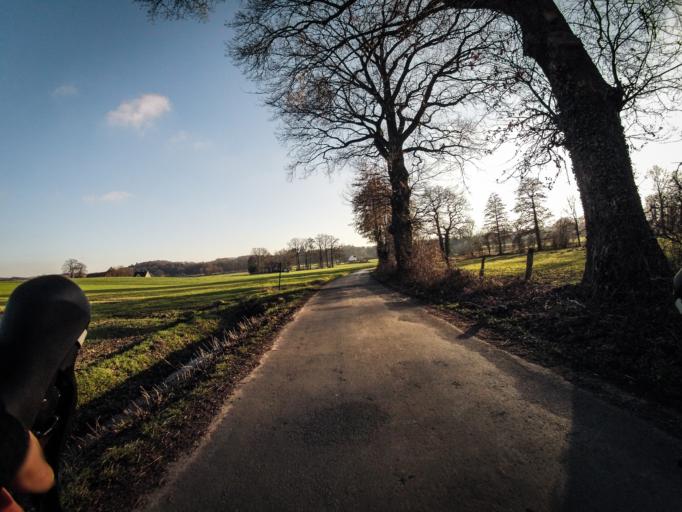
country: DE
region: North Rhine-Westphalia
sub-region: Regierungsbezirk Munster
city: Tecklenburg
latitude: 52.2640
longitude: 7.8006
